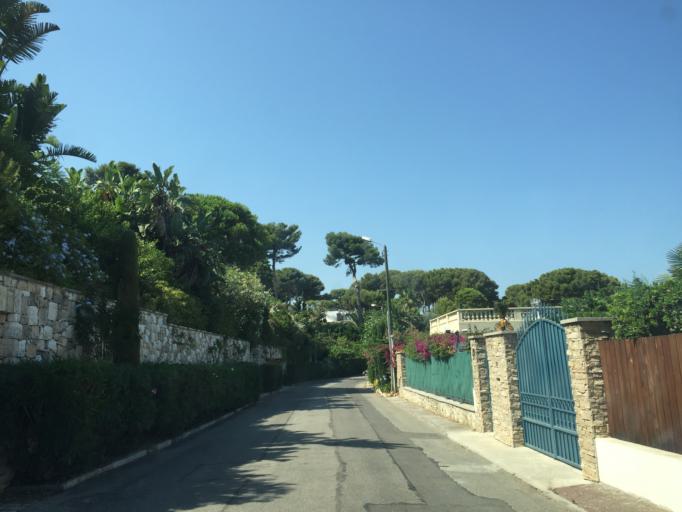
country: FR
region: Provence-Alpes-Cote d'Azur
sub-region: Departement des Alpes-Maritimes
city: Antibes
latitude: 43.5650
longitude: 7.1365
